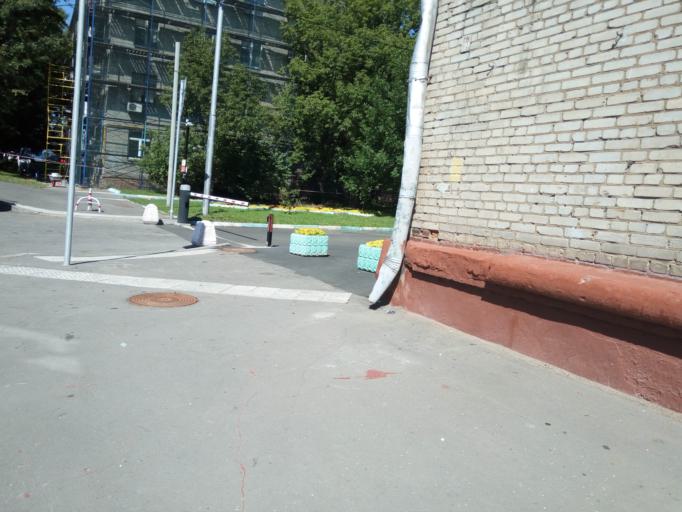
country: RU
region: Moscow
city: Sokol
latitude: 55.7722
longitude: 37.5147
